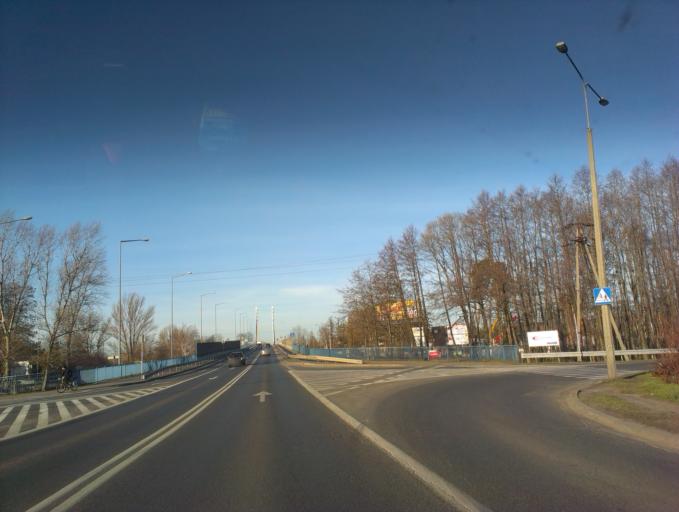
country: PL
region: Greater Poland Voivodeship
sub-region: Powiat poznanski
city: Suchy Las
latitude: 52.4617
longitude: 16.8921
